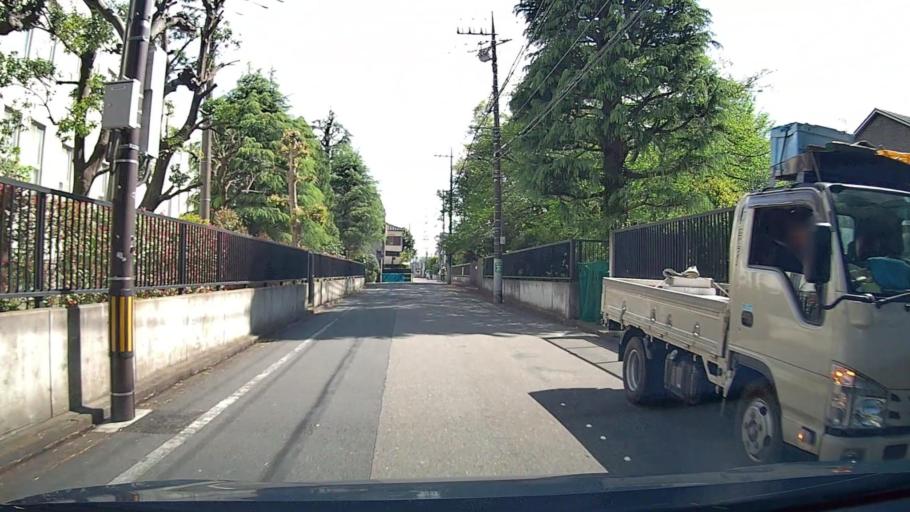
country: JP
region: Tokyo
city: Musashino
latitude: 35.7294
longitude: 139.5820
